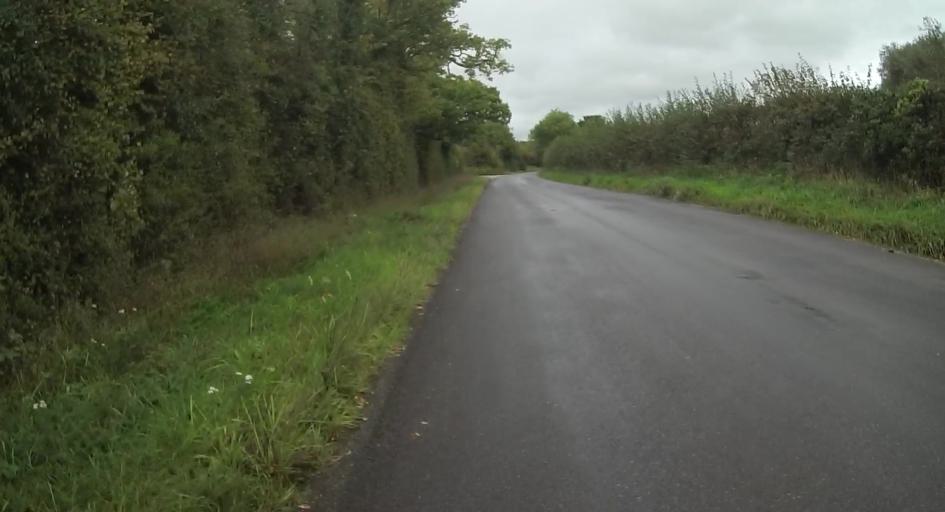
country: GB
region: England
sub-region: Hampshire
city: Tadley
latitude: 51.3859
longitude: -1.1796
